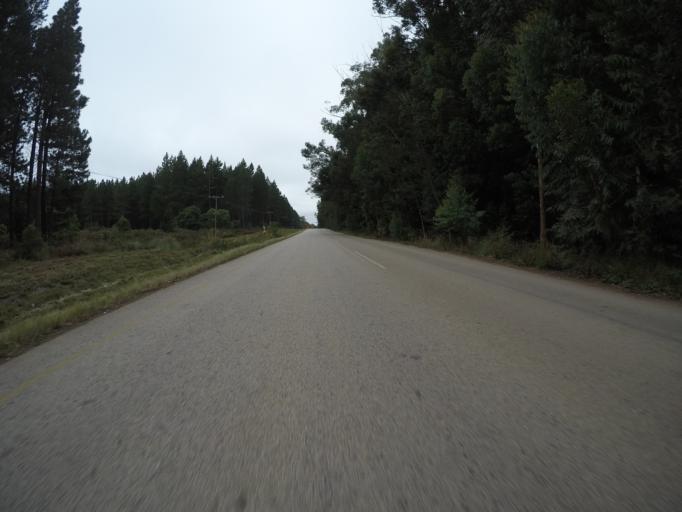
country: ZA
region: Eastern Cape
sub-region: Cacadu District Municipality
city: Kareedouw
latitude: -33.9942
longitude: 24.1107
